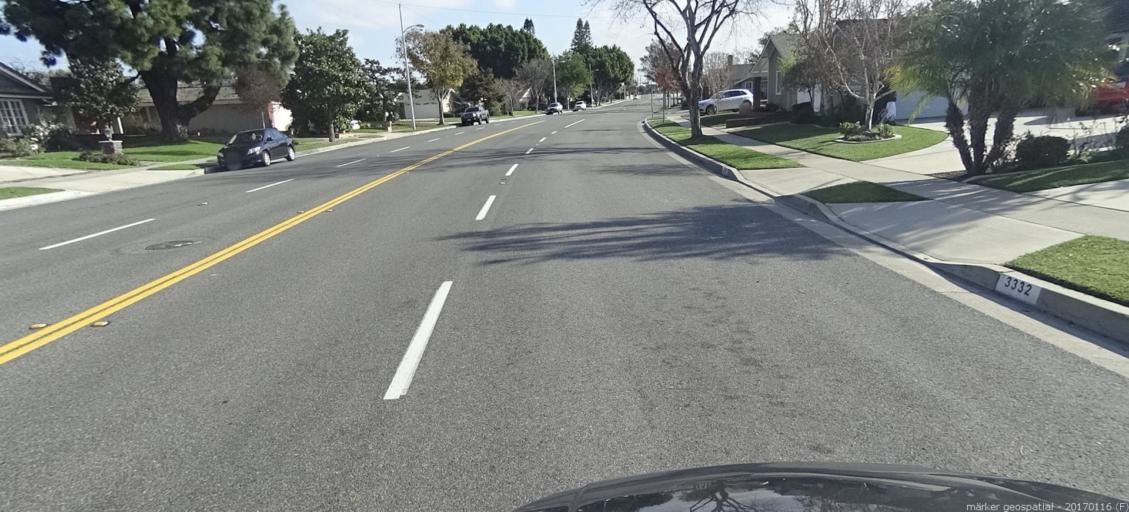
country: US
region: California
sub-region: Orange County
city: Los Alamitos
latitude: 33.7957
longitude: -118.0753
